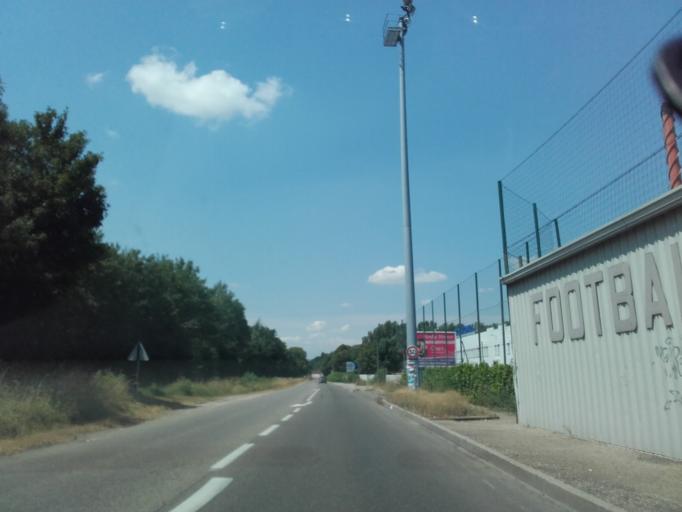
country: FR
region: Rhone-Alpes
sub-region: Departement de l'Isere
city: Bourgoin-Jallieu
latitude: 45.6025
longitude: 5.2652
